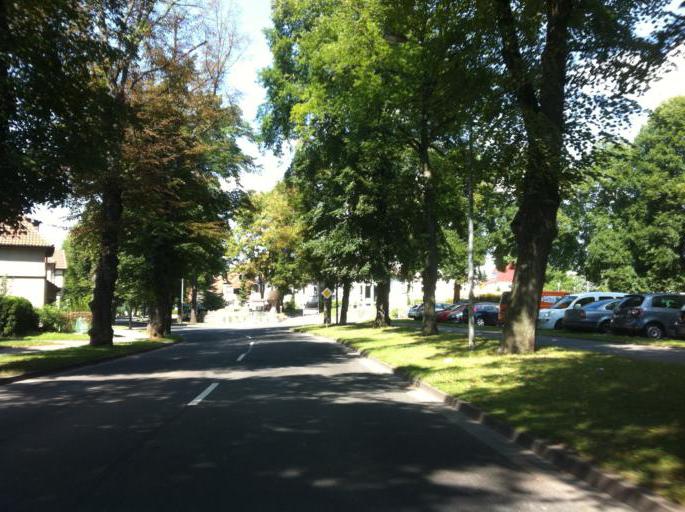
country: DE
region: Thuringia
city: Heilbad Heiligenstadt
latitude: 51.3735
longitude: 10.1496
